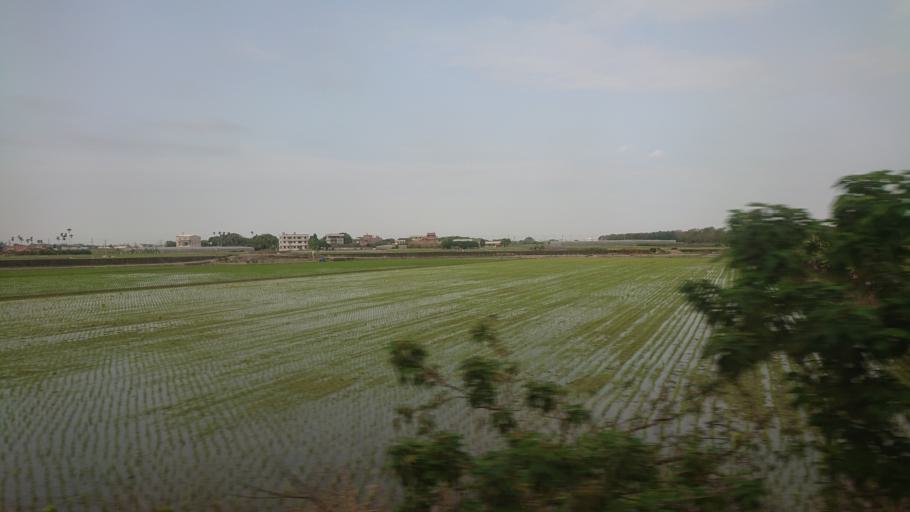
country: TW
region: Taiwan
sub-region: Yunlin
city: Douliu
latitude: 23.7402
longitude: 120.5883
